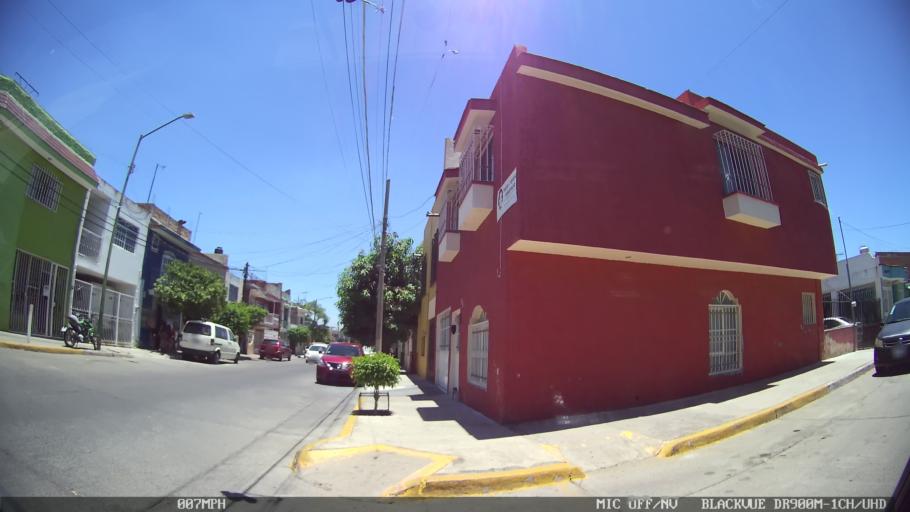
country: MX
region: Jalisco
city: Tlaquepaque
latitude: 20.6709
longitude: -103.2904
